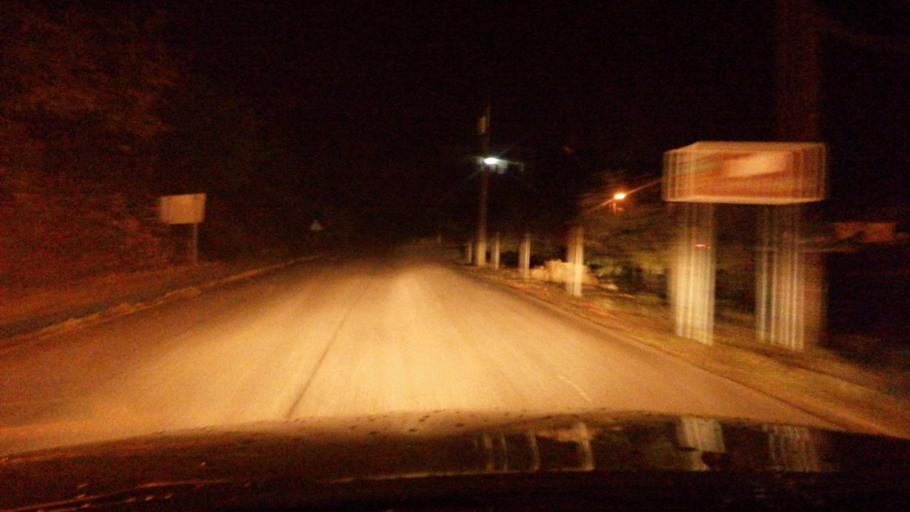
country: PT
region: Viseu
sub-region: Armamar
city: Armamar
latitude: 41.0581
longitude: -7.6461
